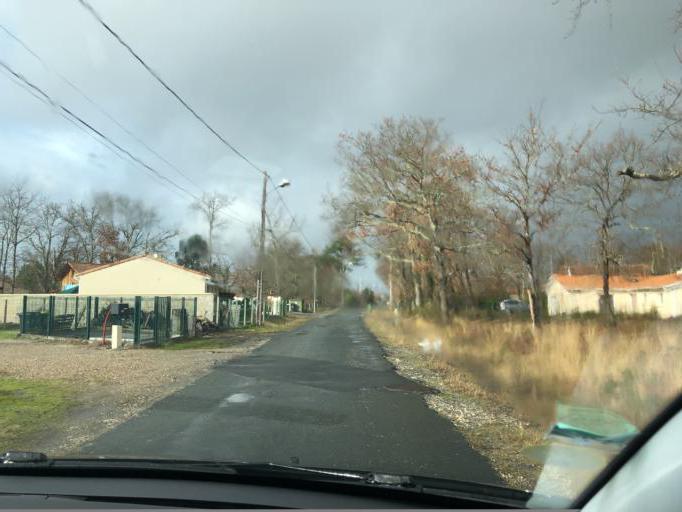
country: FR
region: Aquitaine
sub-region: Departement de la Gironde
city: Hourtin
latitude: 45.1801
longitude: -1.0533
